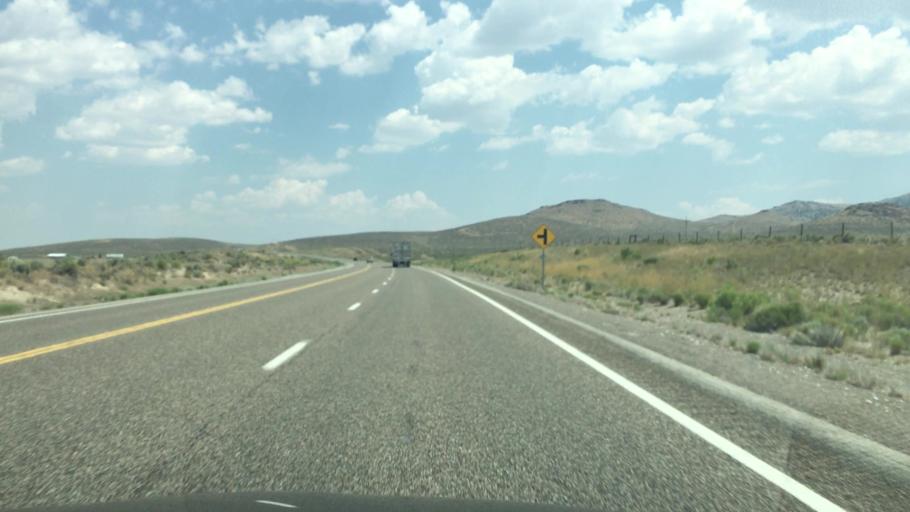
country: US
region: Nevada
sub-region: Elko County
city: Wells
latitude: 41.1723
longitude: -114.8814
